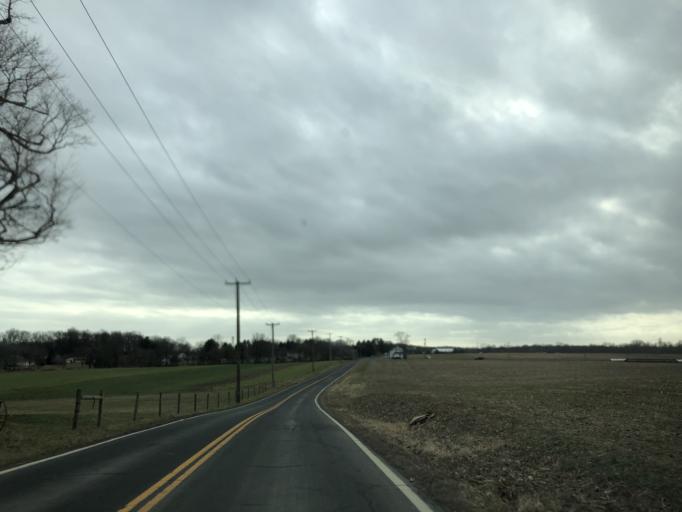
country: US
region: Maryland
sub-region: Cecil County
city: North East
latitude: 39.6779
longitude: -75.9532
